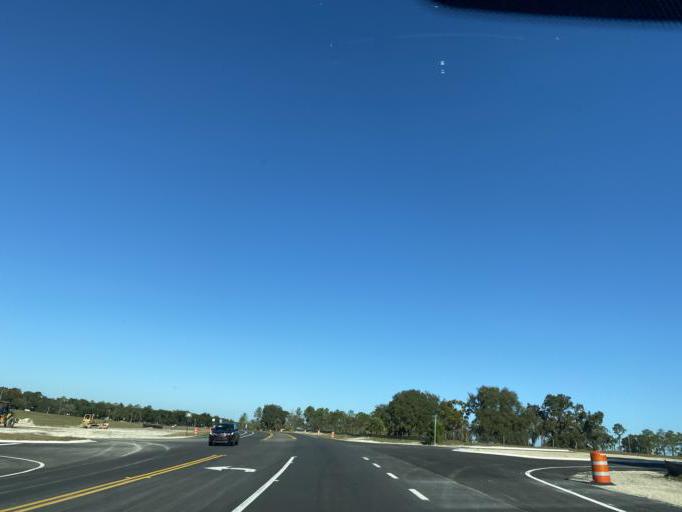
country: US
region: Florida
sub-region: Lake County
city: Mount Plymouth
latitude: 28.8307
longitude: -81.5217
